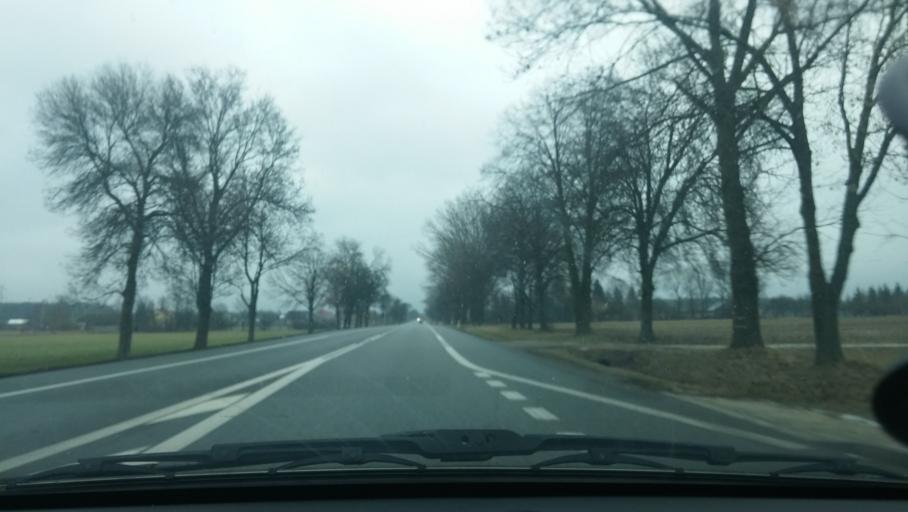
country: PL
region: Masovian Voivodeship
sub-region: Powiat siedlecki
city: Kotun
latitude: 52.1980
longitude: 22.0150
